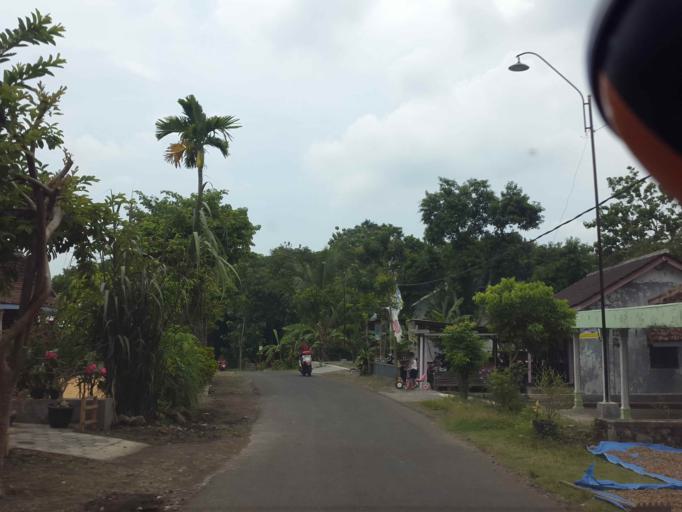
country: ID
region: East Java
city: Ponorogo
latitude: -7.7713
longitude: 111.3485
